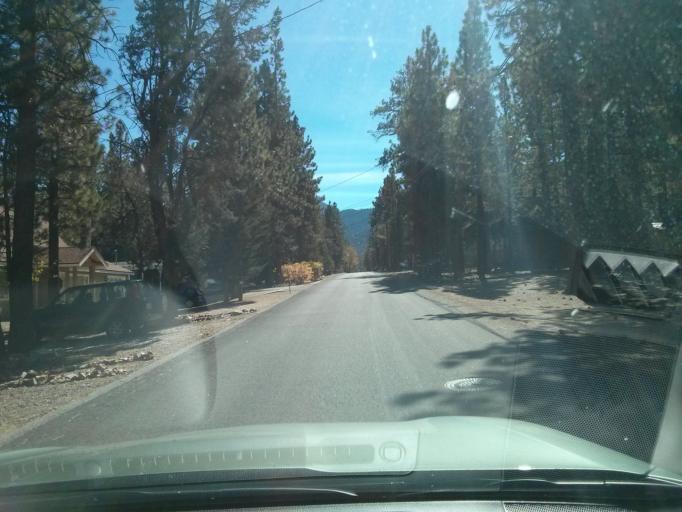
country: US
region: California
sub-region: San Bernardino County
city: Big Bear City
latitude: 34.2483
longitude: -116.8229
